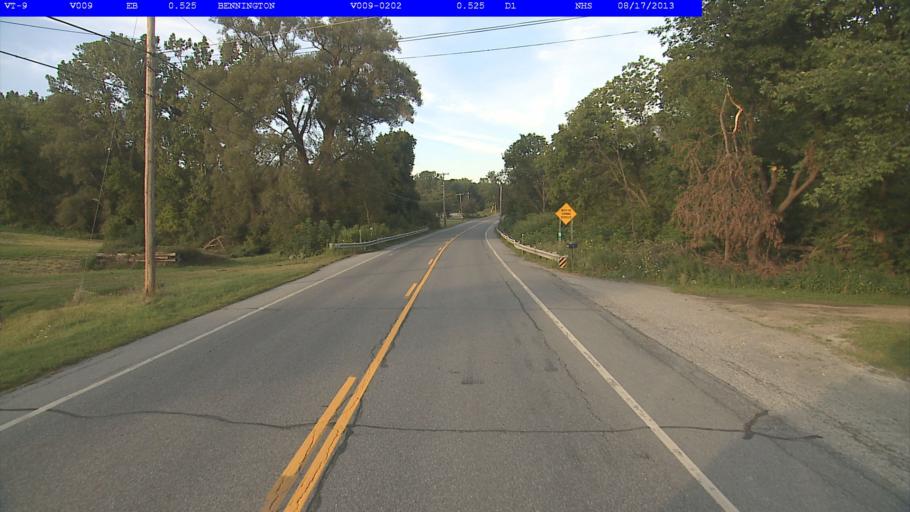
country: US
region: Vermont
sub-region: Bennington County
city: North Bennington
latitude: 42.8755
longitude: -73.2677
